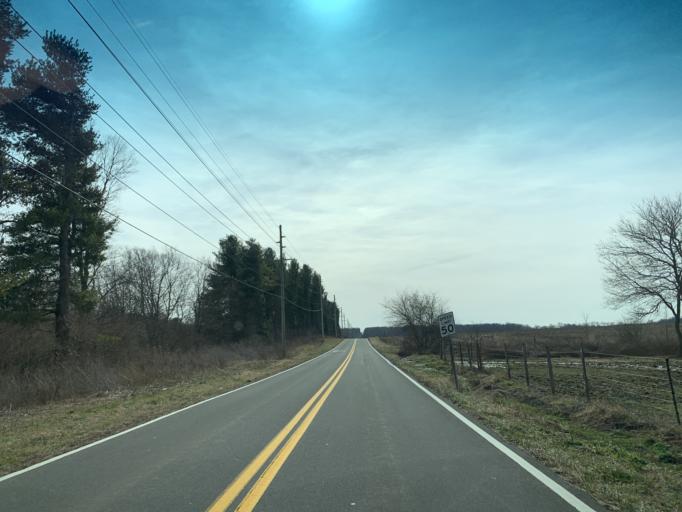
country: US
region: Maryland
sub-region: Frederick County
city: Buckeystown
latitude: 39.3447
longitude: -77.4506
